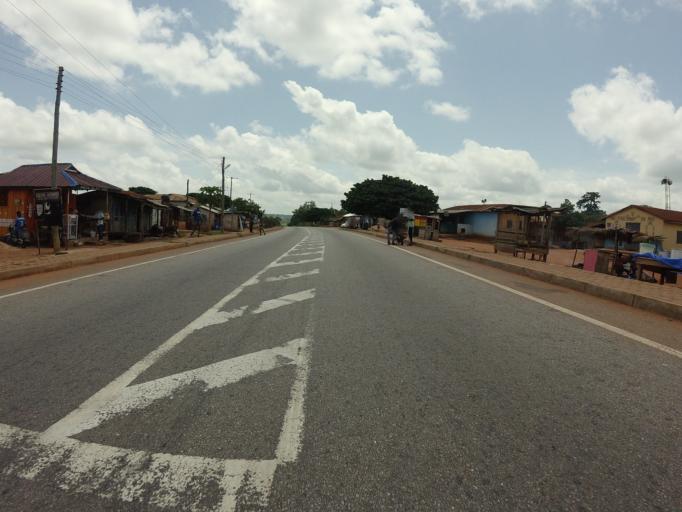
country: GH
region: Brong-Ahafo
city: Techiman
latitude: 7.7015
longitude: -1.8457
